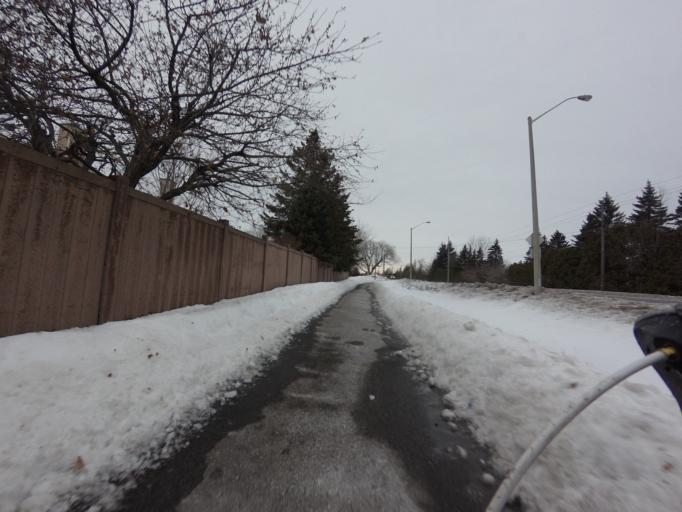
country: CA
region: Ontario
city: Bells Corners
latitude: 45.2745
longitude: -75.7667
